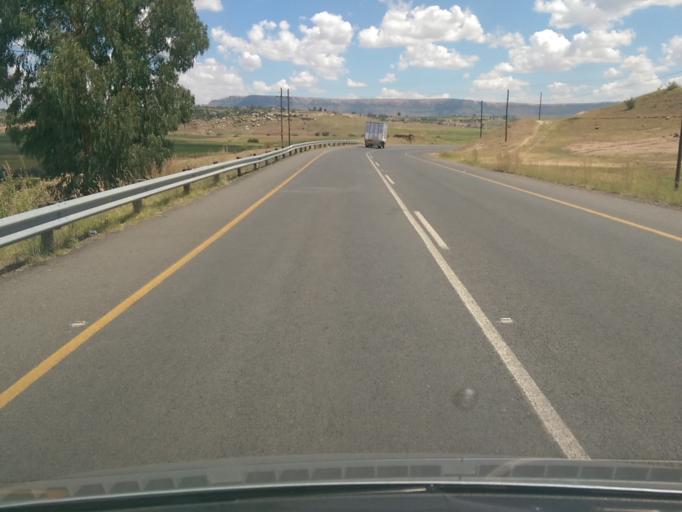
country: LS
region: Maseru
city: Maseru
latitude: -29.3912
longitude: 27.5480
